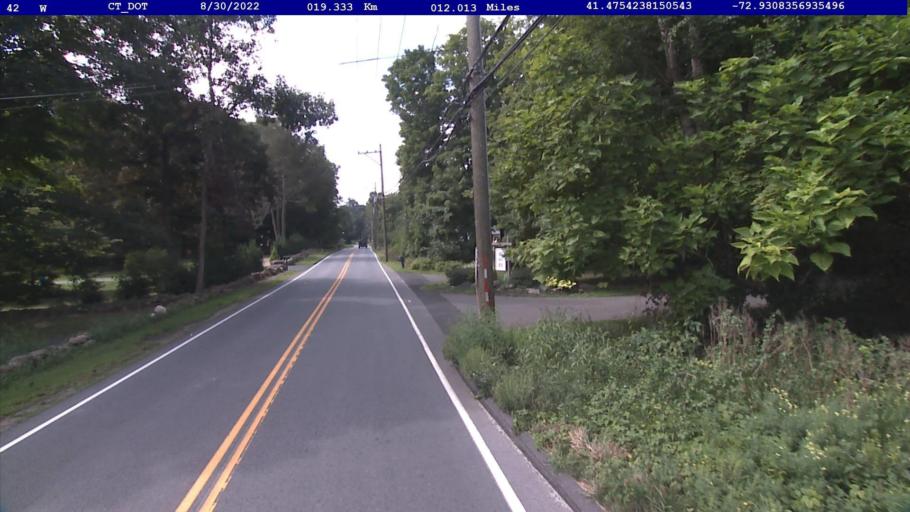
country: US
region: Connecticut
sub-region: New Haven County
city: Cheshire
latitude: 41.4761
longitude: -72.9310
